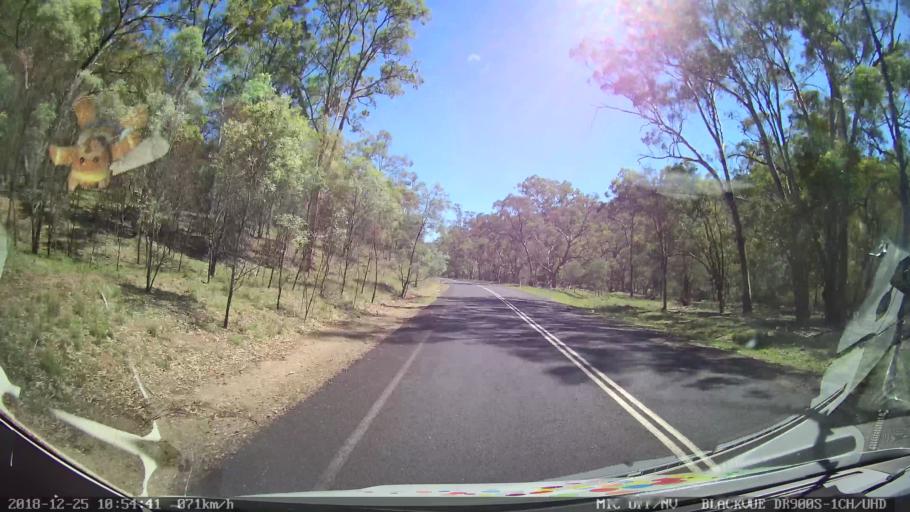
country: AU
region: New South Wales
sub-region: Upper Hunter Shire
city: Merriwa
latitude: -32.4073
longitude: 150.2736
